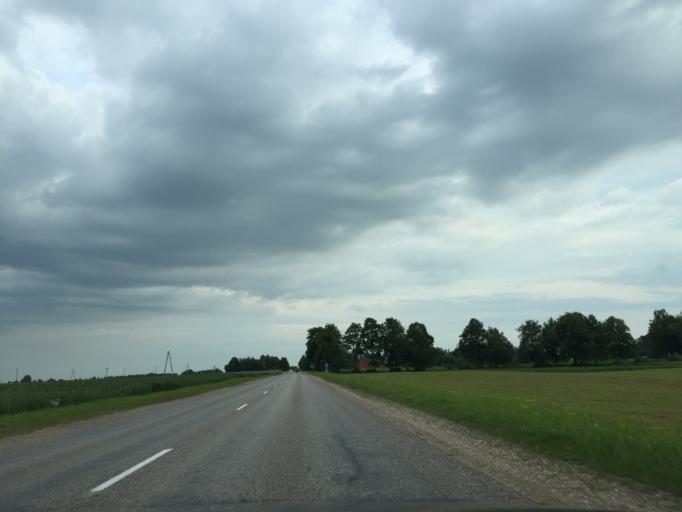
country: LV
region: Dobeles Rajons
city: Dobele
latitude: 56.5717
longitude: 23.2988
